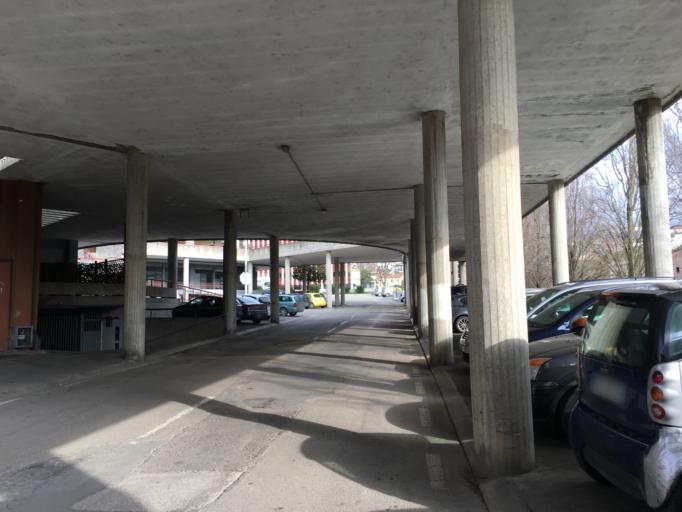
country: IT
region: Umbria
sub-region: Provincia di Perugia
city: Perugia
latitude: 43.1001
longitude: 12.3706
